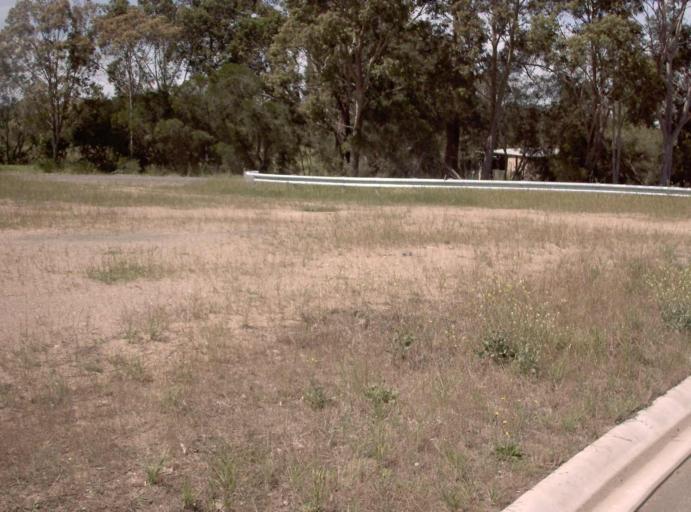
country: AU
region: Victoria
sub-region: Wellington
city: Sale
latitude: -38.1107
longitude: 147.0419
